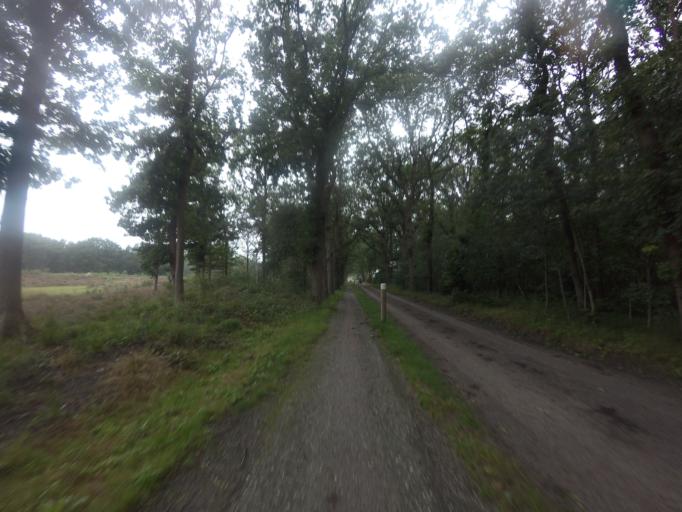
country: NL
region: Friesland
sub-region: Gemeente Heerenveen
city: Nieuwehorne
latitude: 52.9535
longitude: 6.0968
